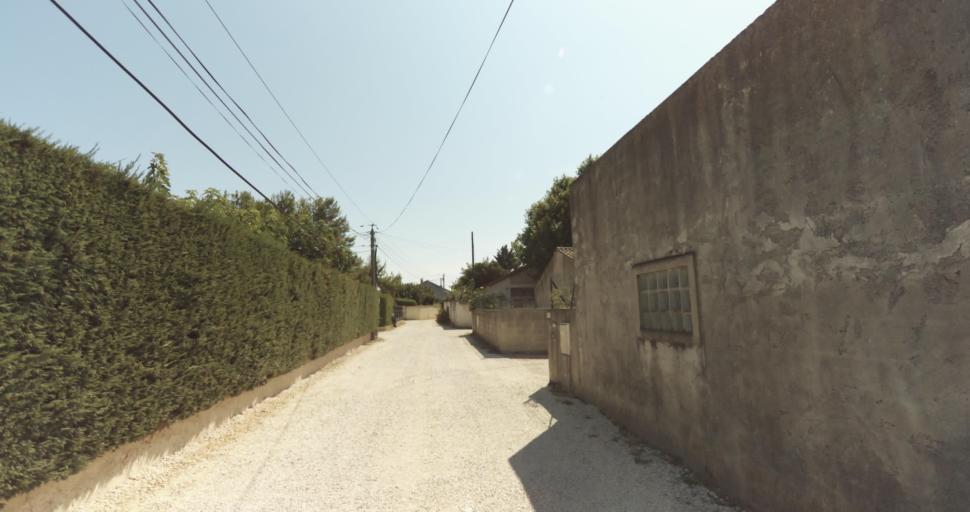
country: FR
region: Provence-Alpes-Cote d'Azur
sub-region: Departement du Vaucluse
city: Monteux
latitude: 44.0280
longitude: 4.9973
